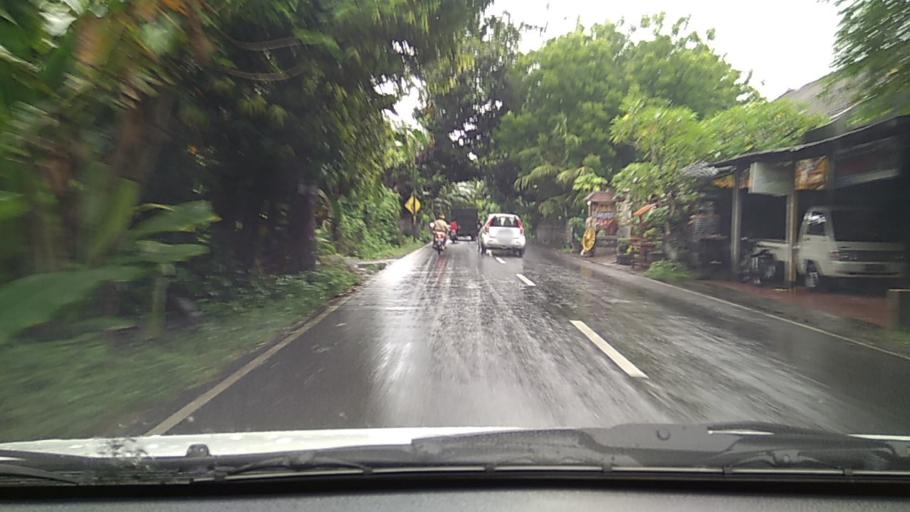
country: ID
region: Bali
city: Banjar Timbrah
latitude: -8.4830
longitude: 115.6062
